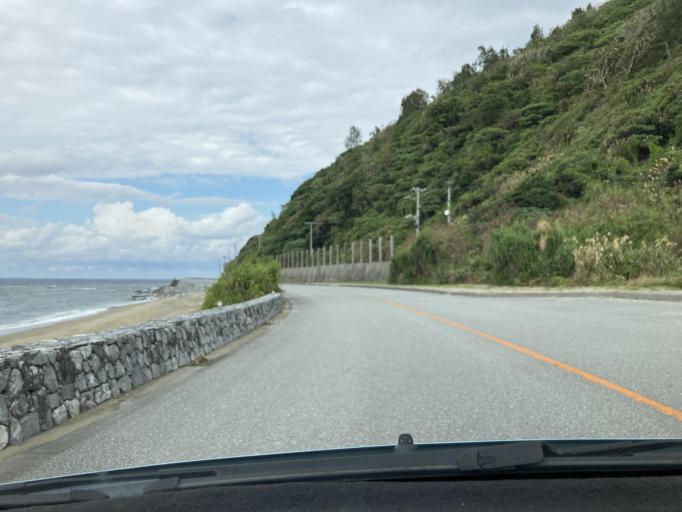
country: JP
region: Okinawa
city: Nago
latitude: 26.7698
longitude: 128.2054
